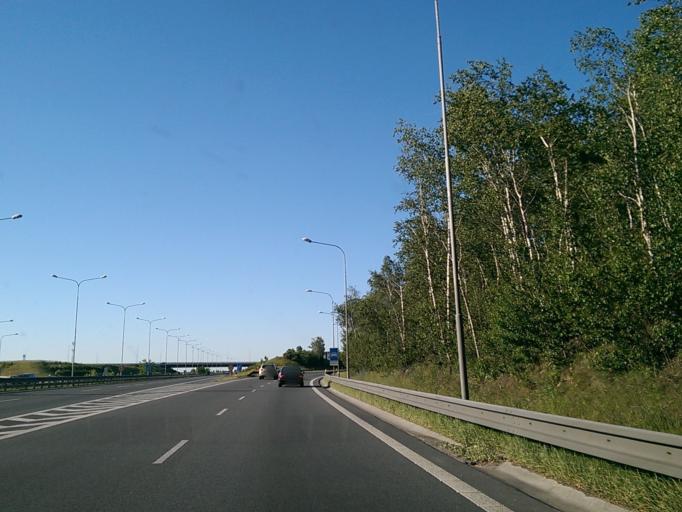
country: CZ
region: Praha
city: Cerny Most
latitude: 50.1149
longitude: 14.5885
